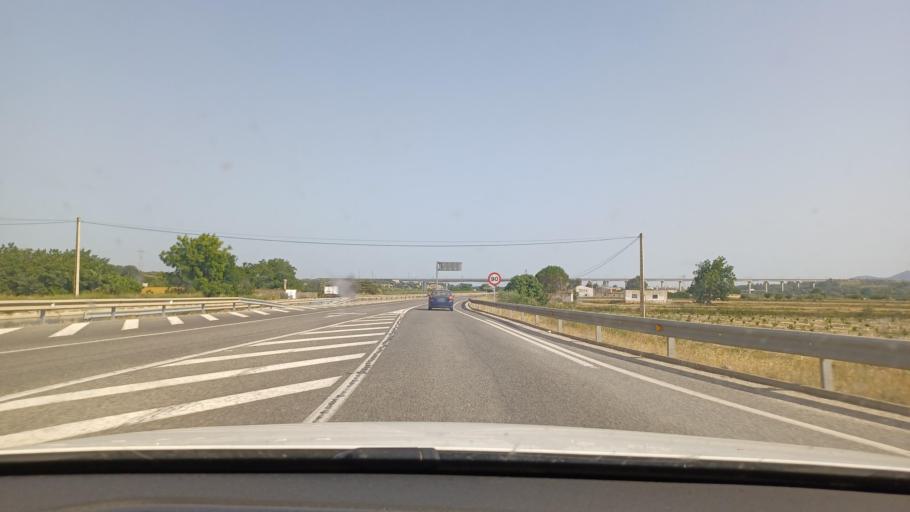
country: ES
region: Catalonia
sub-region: Provincia de Tarragona
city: Amposta
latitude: 40.7416
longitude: 0.5638
